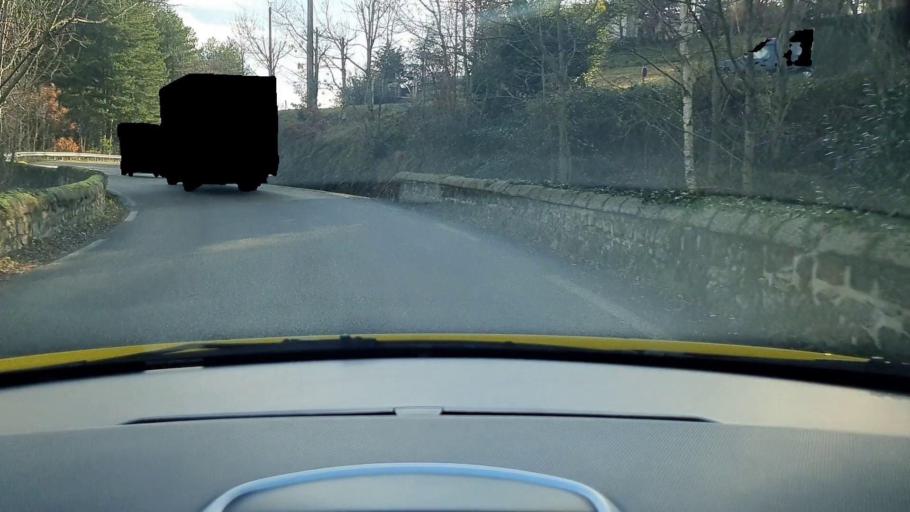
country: FR
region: Languedoc-Roussillon
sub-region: Departement du Gard
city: Branoux-les-Taillades
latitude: 44.3794
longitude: 3.9406
